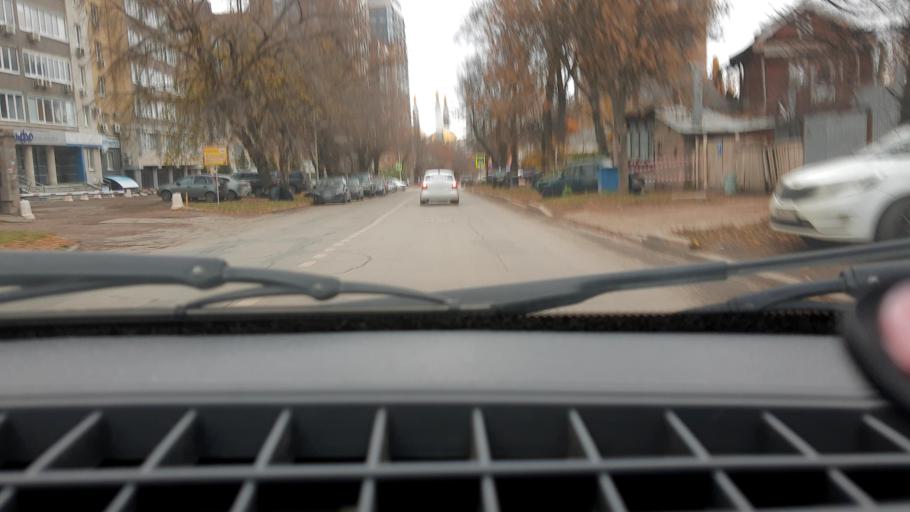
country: RU
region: Bashkortostan
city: Ufa
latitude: 54.7218
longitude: 55.9601
